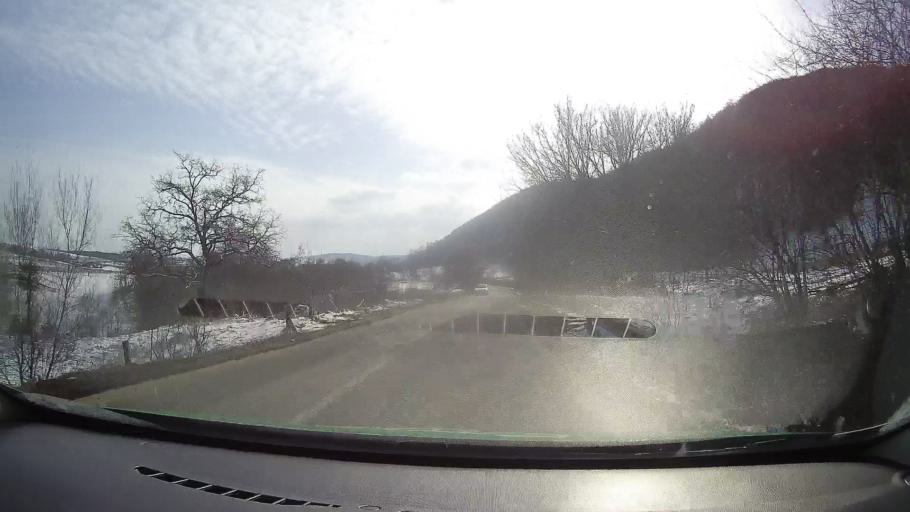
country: RO
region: Mures
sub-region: Municipiul Sighisoara
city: Sighisoara
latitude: 46.1961
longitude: 24.7651
